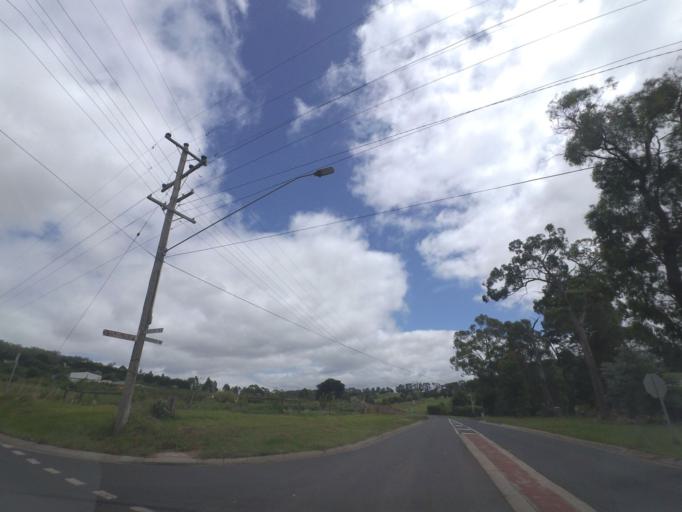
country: AU
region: Victoria
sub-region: Yarra Ranges
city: Mount Evelyn
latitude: -37.7950
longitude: 145.4569
